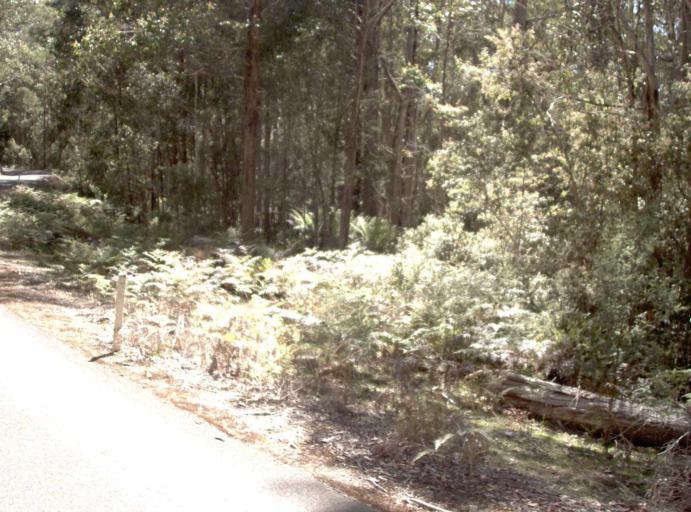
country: AU
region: New South Wales
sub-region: Bombala
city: Bombala
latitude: -37.0739
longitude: 148.7805
